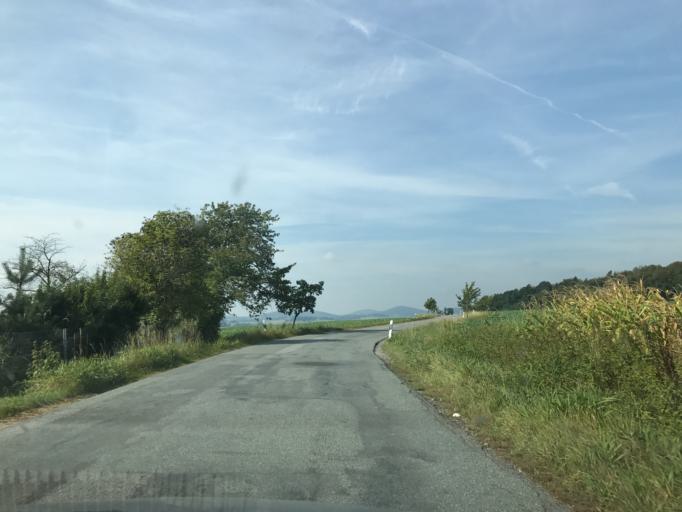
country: DE
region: Saxony
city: Lobau
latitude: 51.0828
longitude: 14.6942
